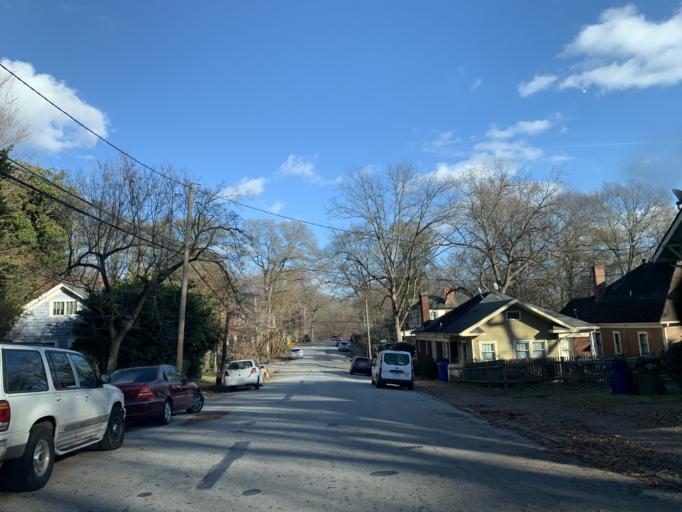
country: US
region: Georgia
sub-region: Fulton County
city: Atlanta
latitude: 33.7412
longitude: -84.3756
